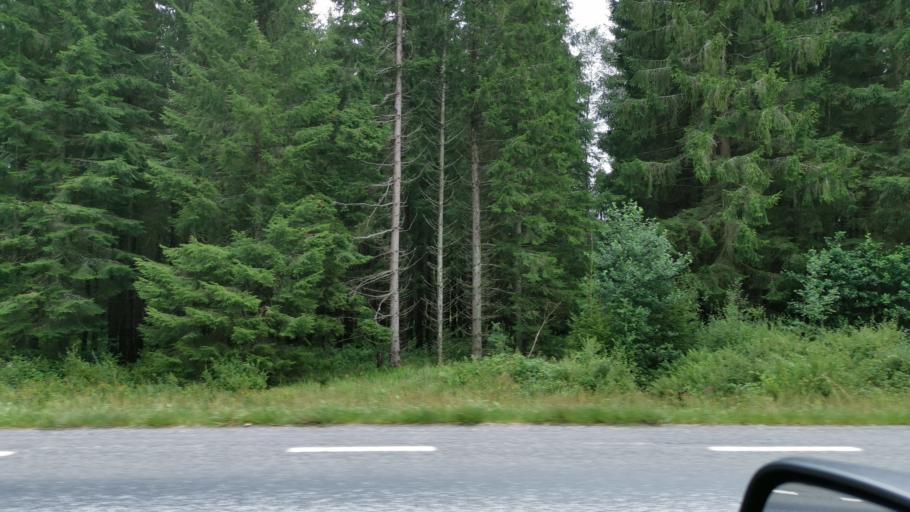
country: SE
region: Vaestra Goetaland
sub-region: Trollhattan
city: Trollhattan
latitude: 58.3278
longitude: 12.1858
